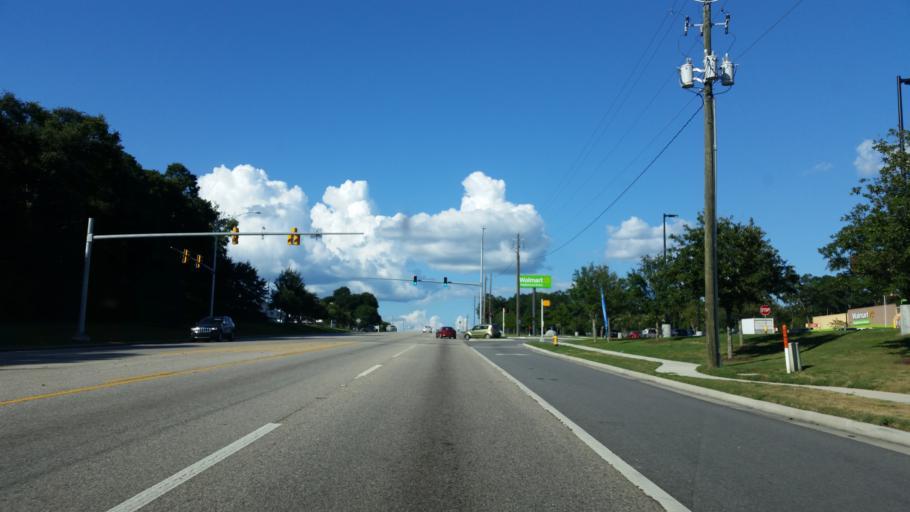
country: US
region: Alabama
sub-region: Mobile County
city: Prichard
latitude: 30.7167
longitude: -88.1650
